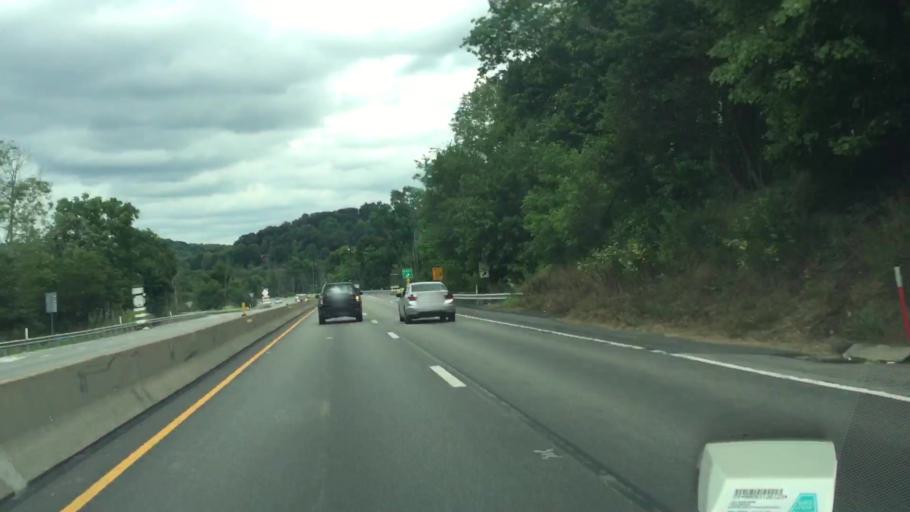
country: US
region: Pennsylvania
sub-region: Allegheny County
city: Franklin Park
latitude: 40.5765
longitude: -80.0349
